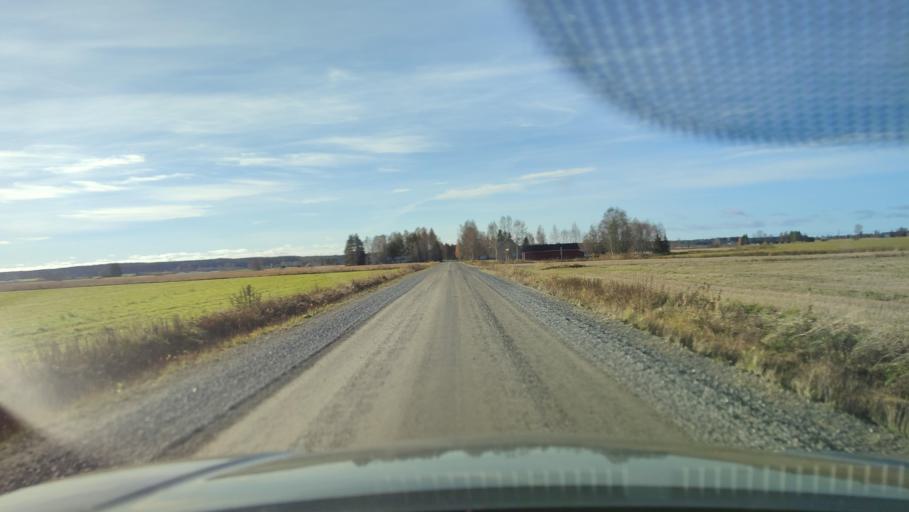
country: FI
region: Southern Ostrobothnia
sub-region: Suupohja
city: Teuva
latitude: 62.4657
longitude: 21.7029
